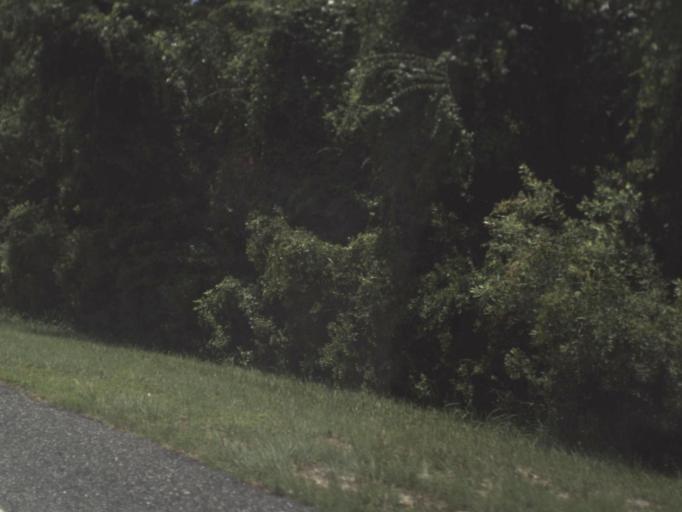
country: US
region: Florida
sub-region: Taylor County
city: Steinhatchee
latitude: 29.7320
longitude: -83.3145
